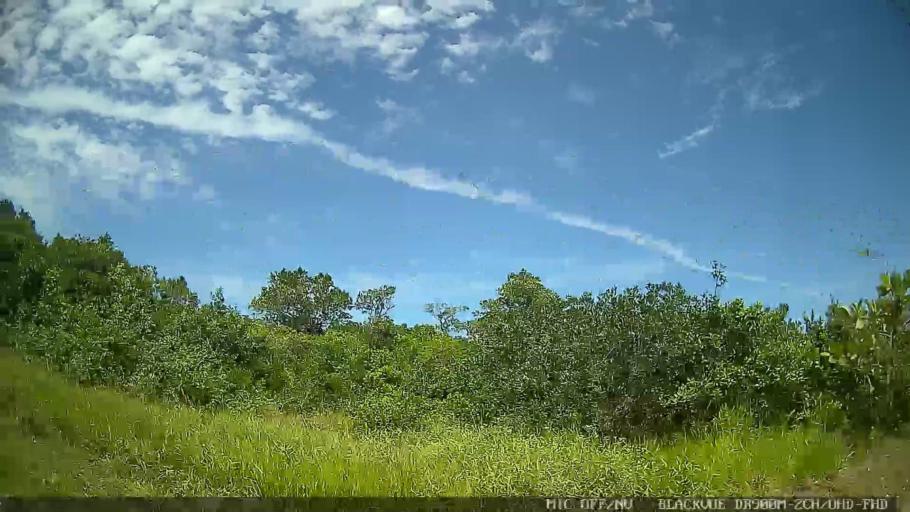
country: BR
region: Sao Paulo
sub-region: Iguape
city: Iguape
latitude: -24.7150
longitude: -47.5180
